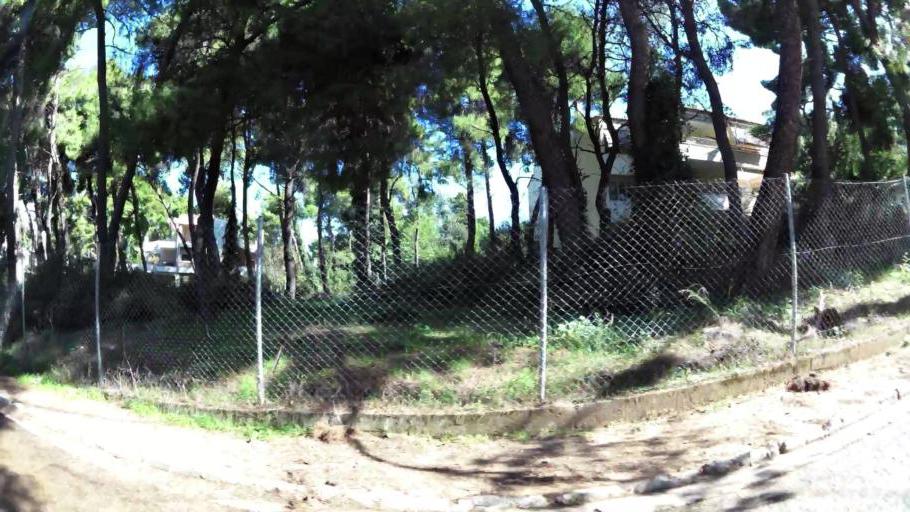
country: GR
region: Attica
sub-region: Nomarchia Anatolikis Attikis
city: Drosia
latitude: 38.1184
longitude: 23.8582
